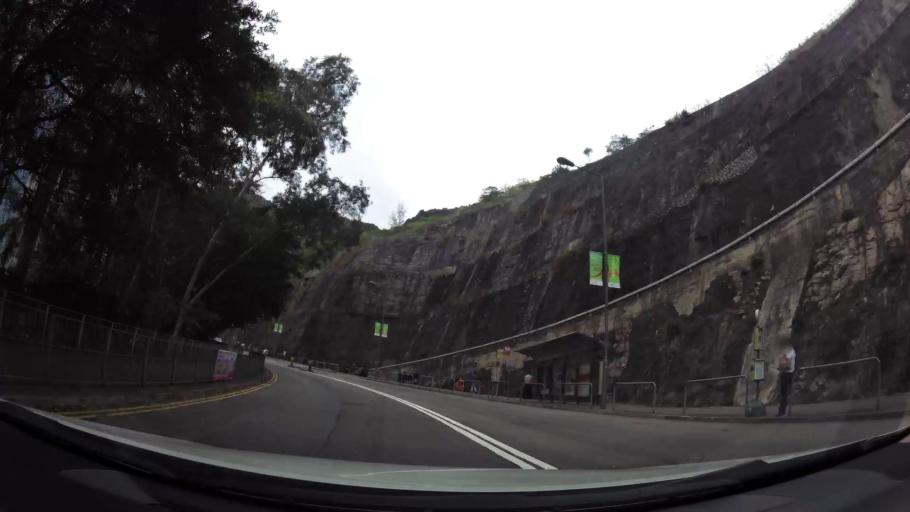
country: HK
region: Wanchai
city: Wan Chai
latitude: 22.2804
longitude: 114.2182
